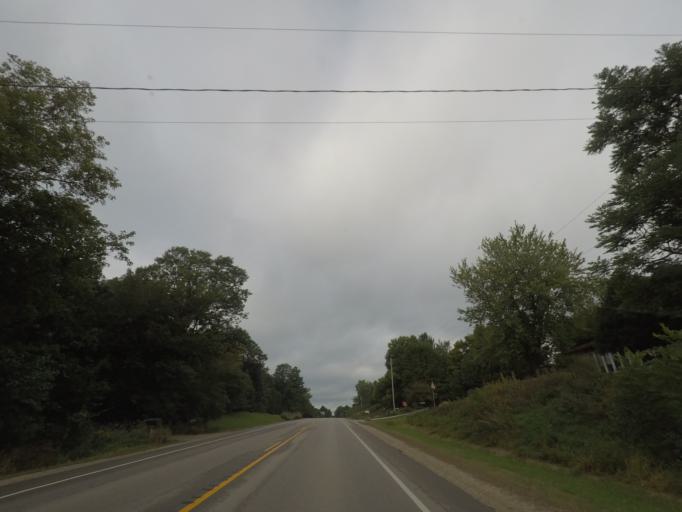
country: US
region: Wisconsin
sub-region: Jefferson County
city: Lake Ripley
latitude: 43.0119
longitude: -88.9750
